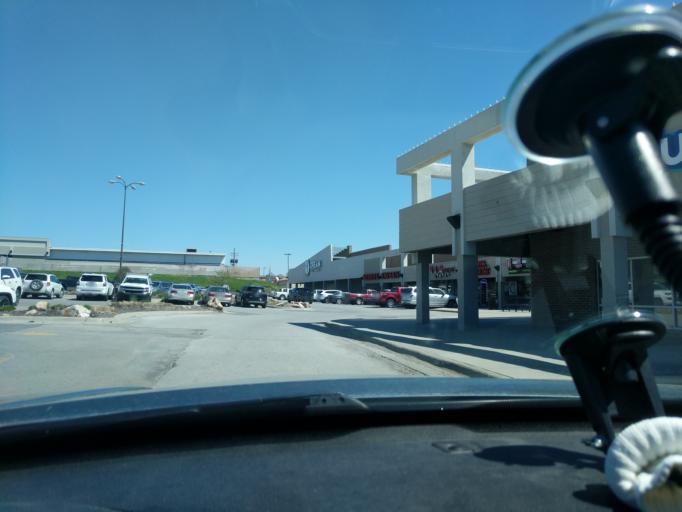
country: US
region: Nebraska
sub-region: Douglas County
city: Ralston
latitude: 41.2334
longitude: -96.0460
